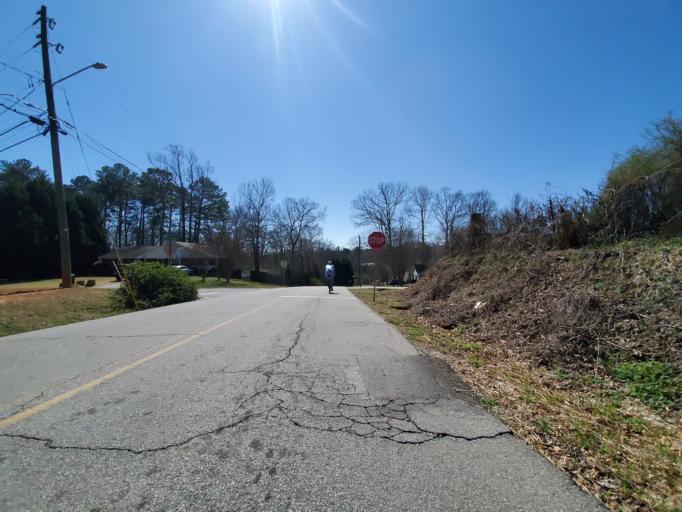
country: US
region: Georgia
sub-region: Barrow County
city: Winder
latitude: 33.9961
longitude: -83.7039
